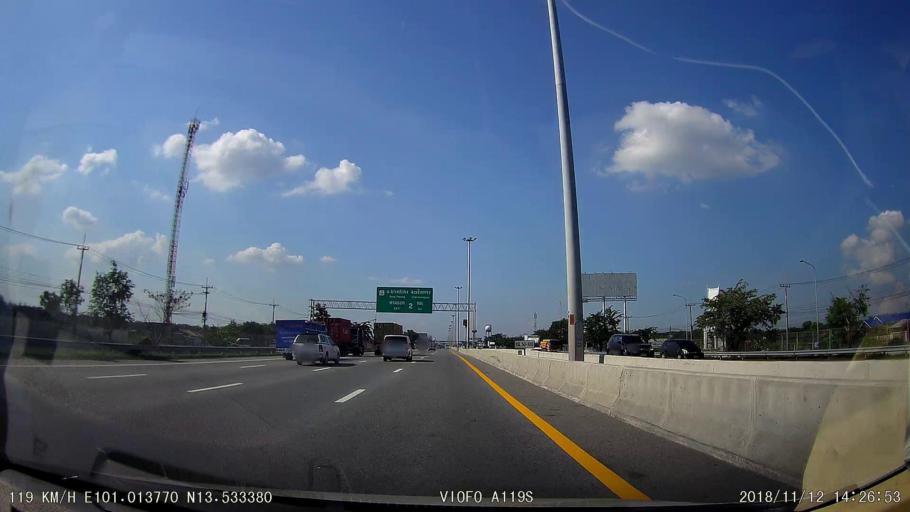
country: TH
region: Chachoengsao
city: Bang Pakong
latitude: 13.5333
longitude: 101.0138
